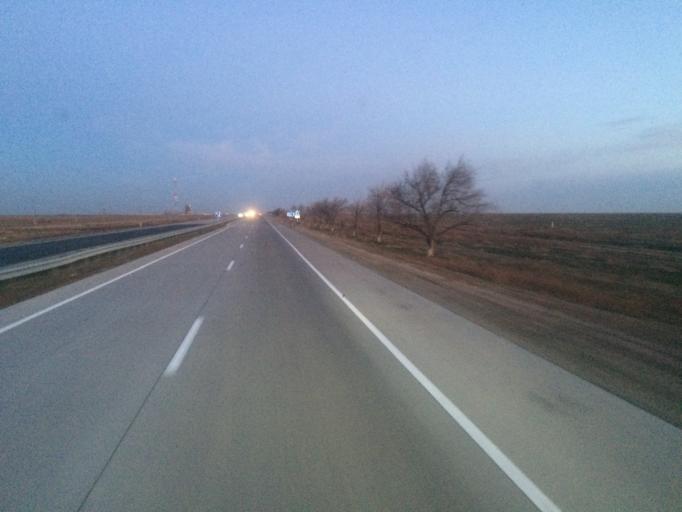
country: KZ
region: Ongtustik Qazaqstan
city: Temirlanovka
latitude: 42.8354
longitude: 69.1171
